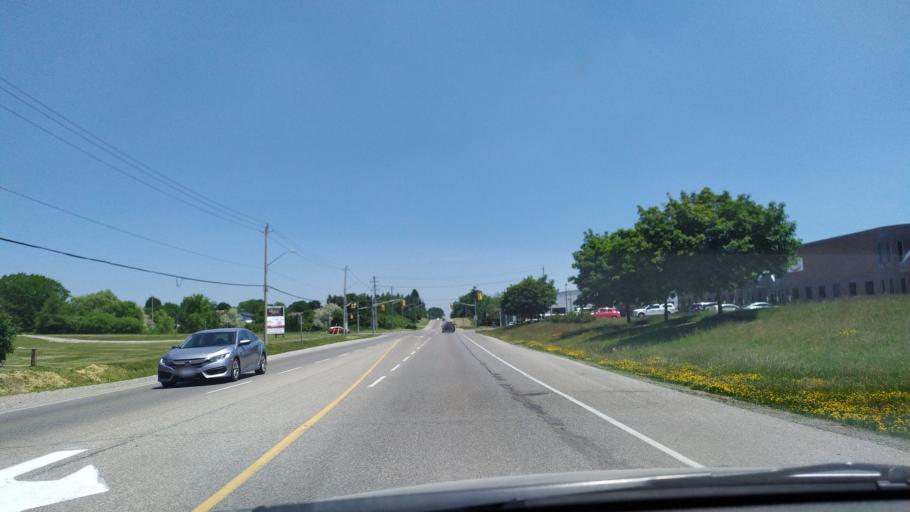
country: CA
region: Ontario
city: Kitchener
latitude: 43.4038
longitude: -80.4877
